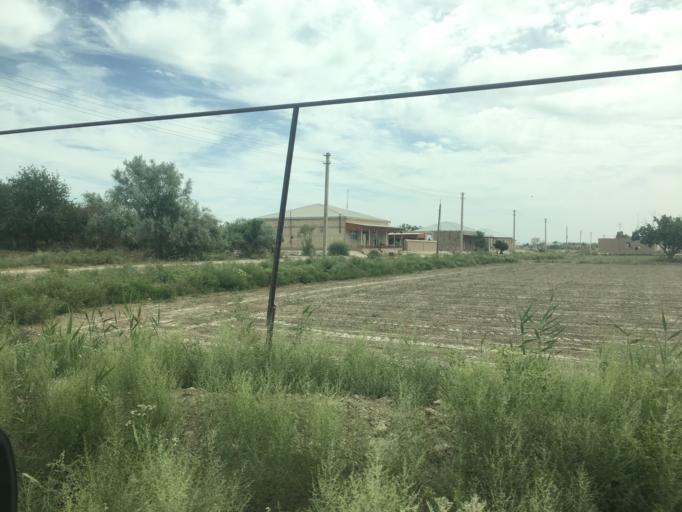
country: TM
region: Dasoguz
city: Tagta
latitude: 41.6117
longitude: 59.8340
